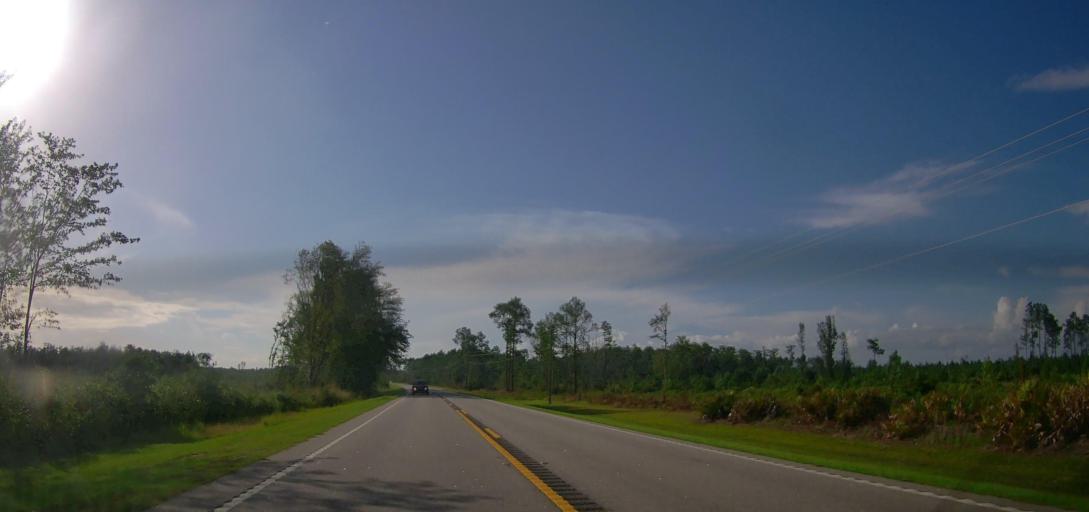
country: US
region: Georgia
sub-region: Coffee County
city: Nicholls
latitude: 31.3805
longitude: -82.6433
